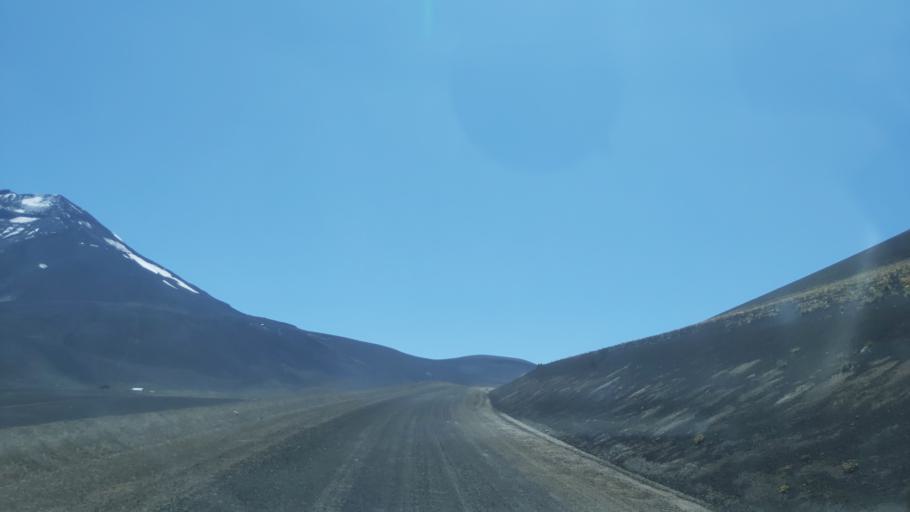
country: CL
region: Araucania
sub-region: Provincia de Cautin
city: Vilcun
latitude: -38.4056
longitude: -71.5434
